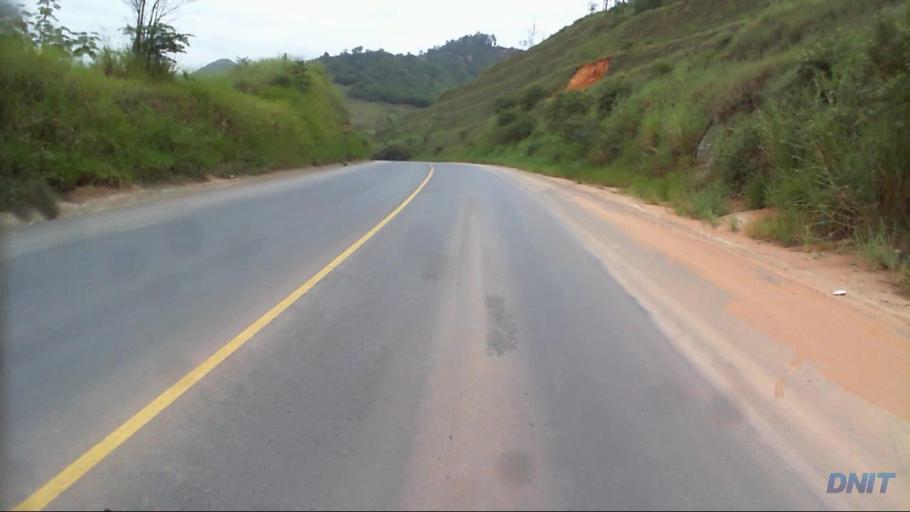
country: BR
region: Minas Gerais
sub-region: Coronel Fabriciano
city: Coronel Fabriciano
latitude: -19.5271
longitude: -42.6694
